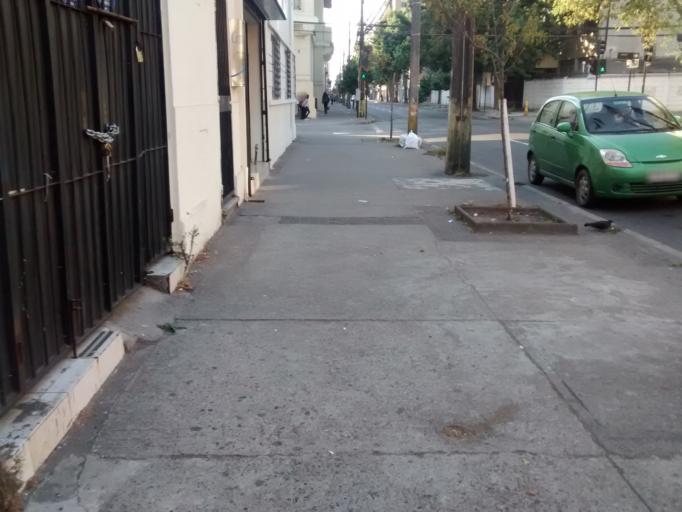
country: CL
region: Biobio
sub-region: Provincia de Concepcion
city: Concepcion
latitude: -36.8306
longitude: -73.0503
